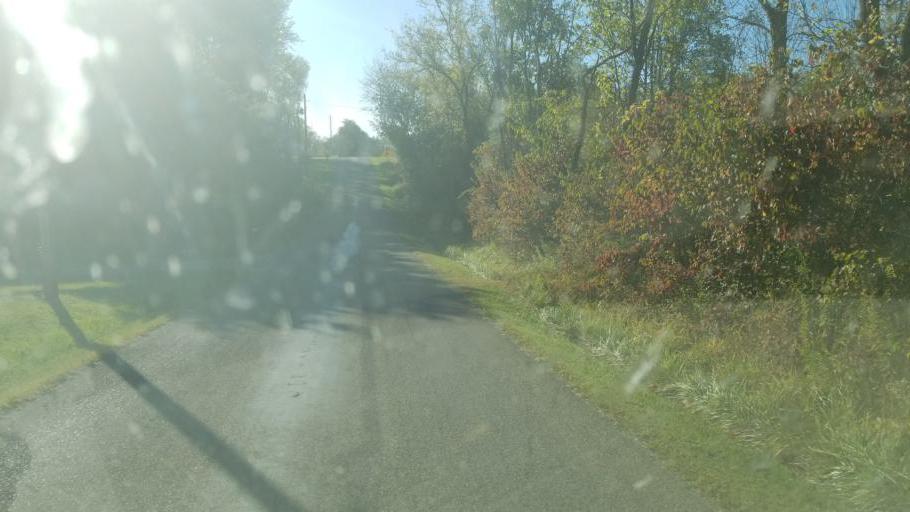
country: US
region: Ohio
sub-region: Richland County
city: Lexington
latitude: 40.6373
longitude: -82.6356
